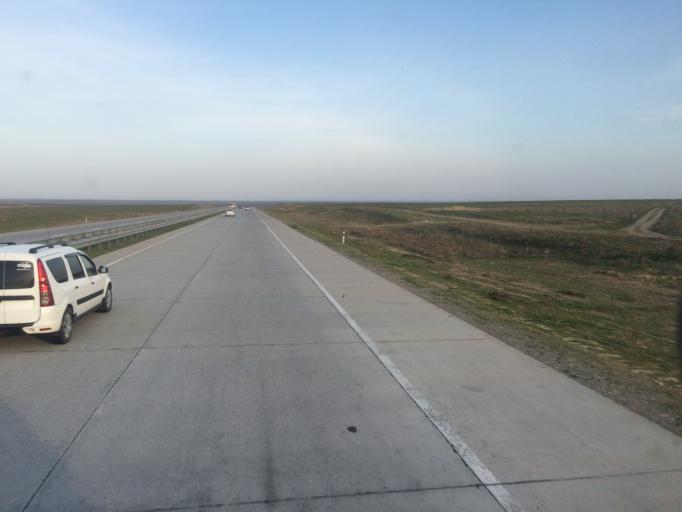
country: KZ
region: Ongtustik Qazaqstan
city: Temirlanovka
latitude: 42.6463
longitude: 69.2472
